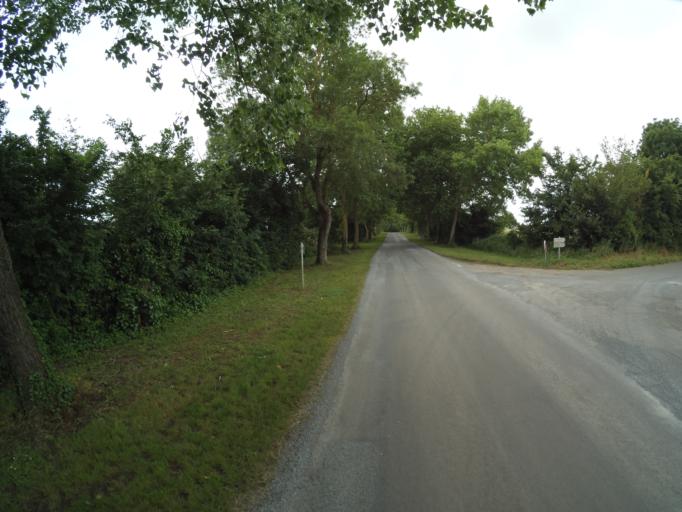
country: FR
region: Poitou-Charentes
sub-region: Departement de la Charente-Maritime
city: Saint-Laurent-de-la-Pree
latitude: 45.9869
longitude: -1.0122
